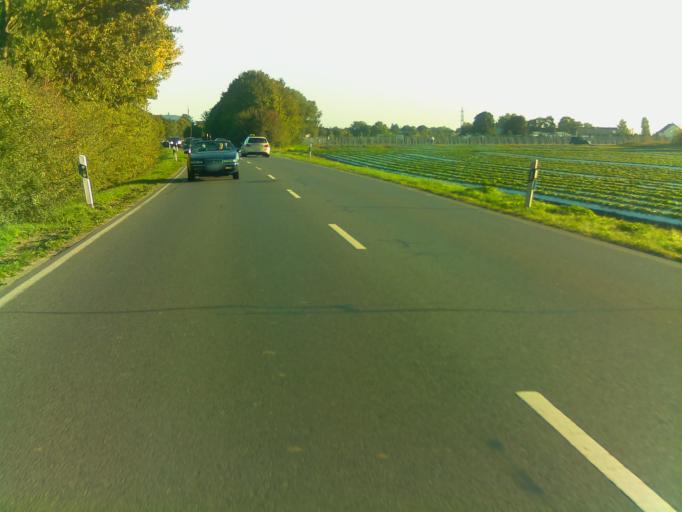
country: DE
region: Hesse
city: Zwingenberg
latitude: 49.7118
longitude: 8.6065
